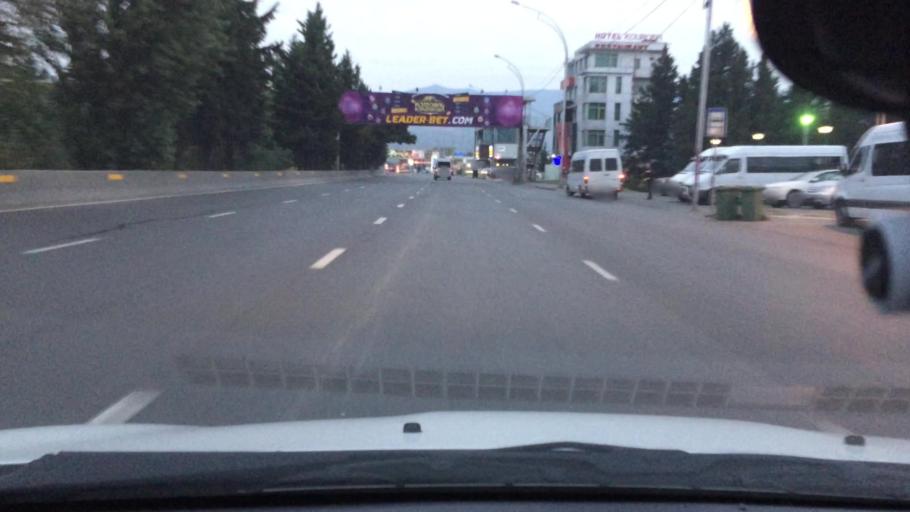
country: GE
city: Zahesi
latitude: 41.7809
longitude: 44.7694
